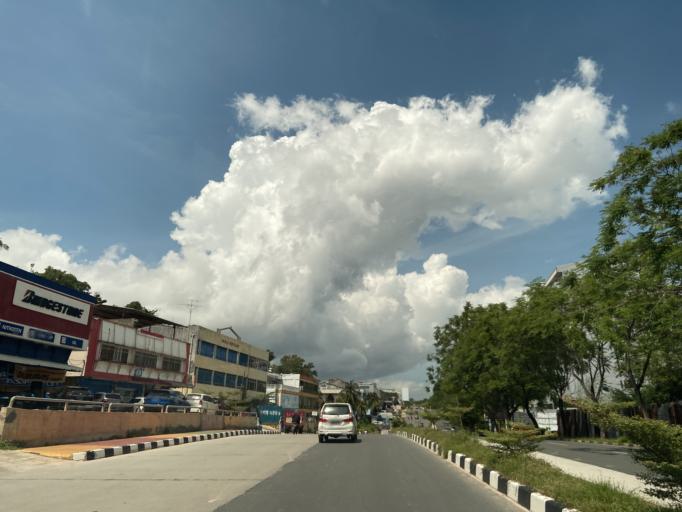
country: SG
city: Singapore
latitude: 1.1389
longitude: 104.0161
